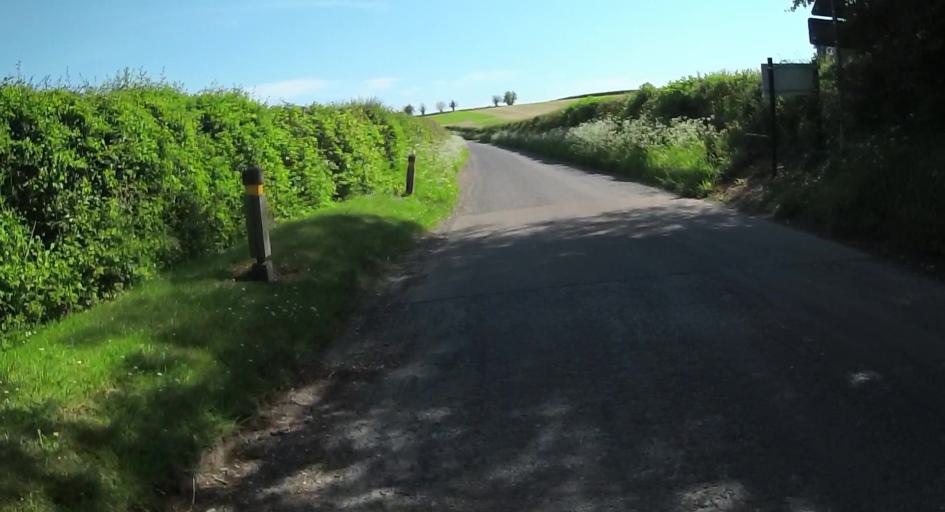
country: GB
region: England
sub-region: Hampshire
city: Kings Worthy
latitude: 51.0828
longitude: -1.2724
